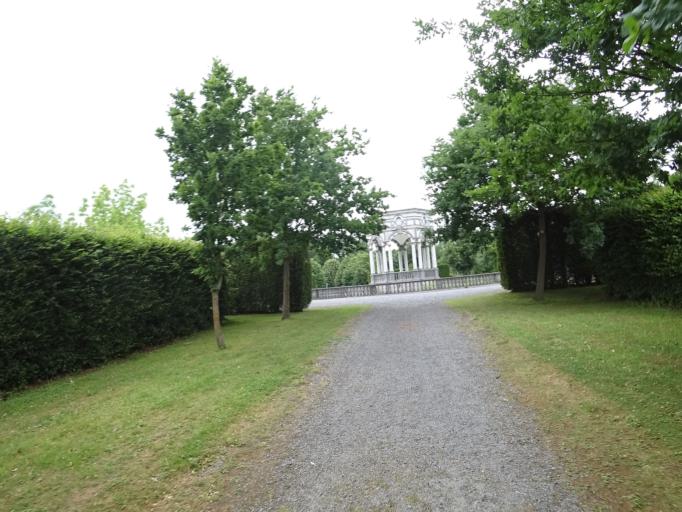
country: BE
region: Wallonia
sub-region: Province du Hainaut
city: Enghien
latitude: 50.6872
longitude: 4.0476
